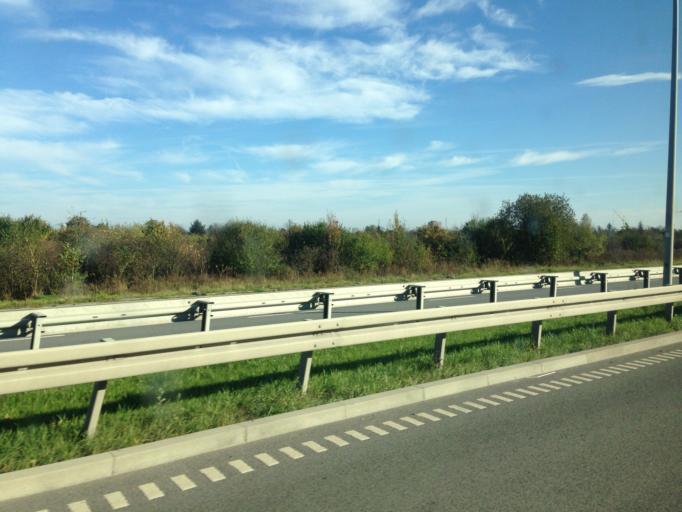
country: PL
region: Pomeranian Voivodeship
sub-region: Gdansk
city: Gdansk
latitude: 54.3639
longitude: 18.6895
